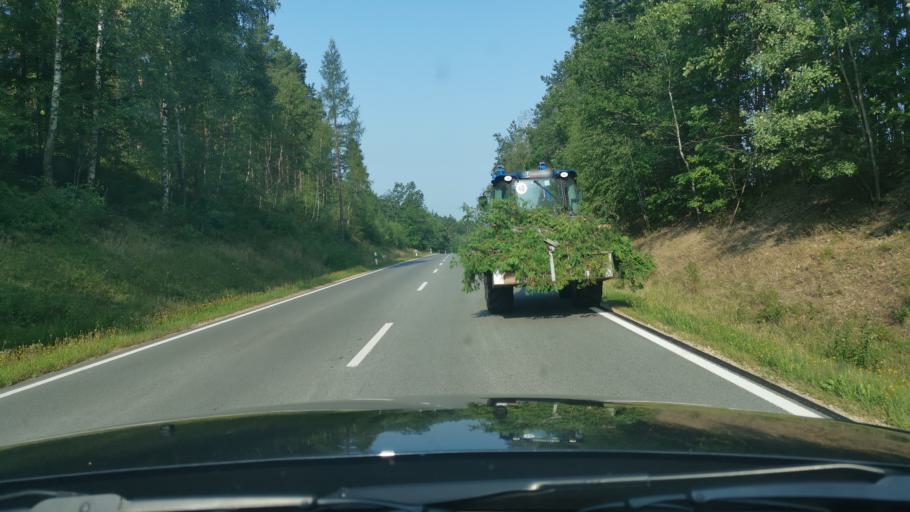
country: DE
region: Bavaria
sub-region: Upper Palatinate
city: Schnaittenbach
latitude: 49.5477
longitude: 12.0474
